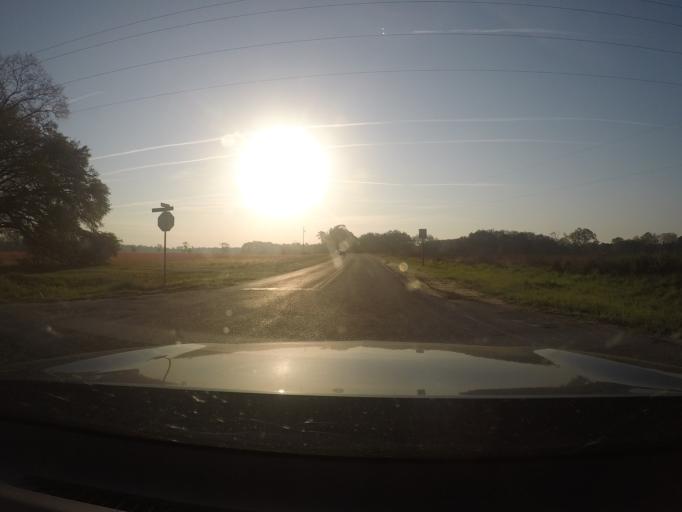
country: US
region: Georgia
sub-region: Bulloch County
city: Brooklet
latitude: 32.2951
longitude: -81.7091
